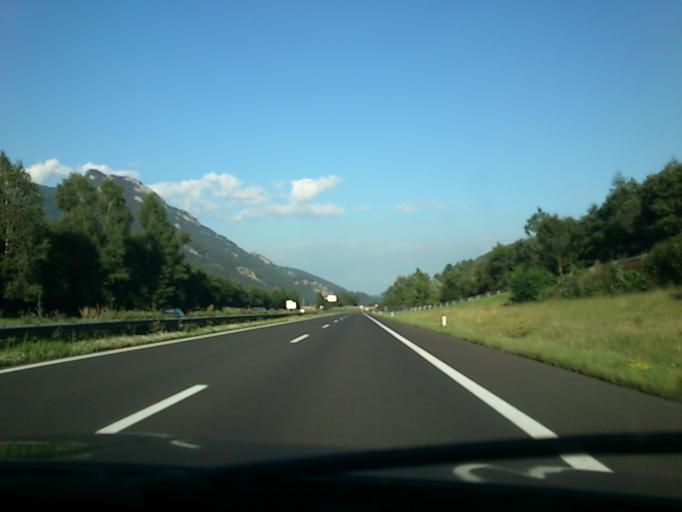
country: AT
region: Styria
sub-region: Politischer Bezirk Leoben
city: Mautern in Steiermark
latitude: 47.3963
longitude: 14.8150
